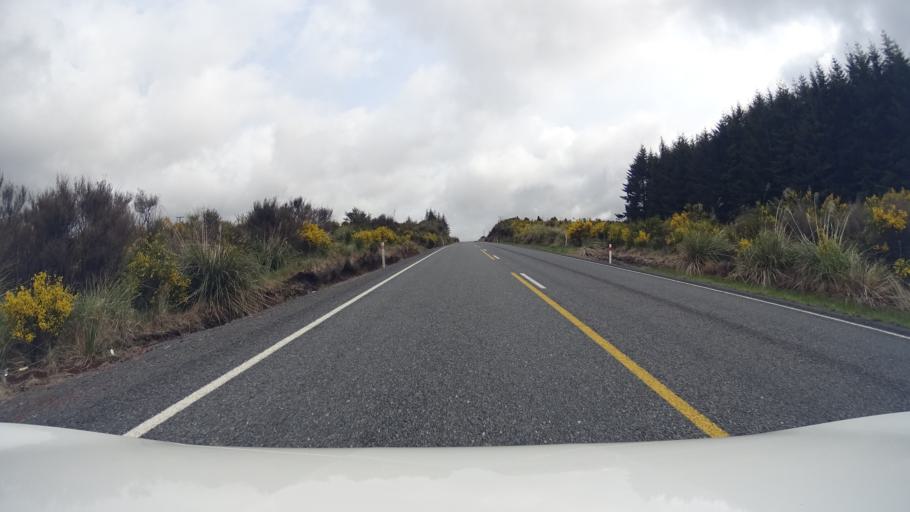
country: NZ
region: Manawatu-Wanganui
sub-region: Ruapehu District
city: Waiouru
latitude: -39.2001
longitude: 175.4012
